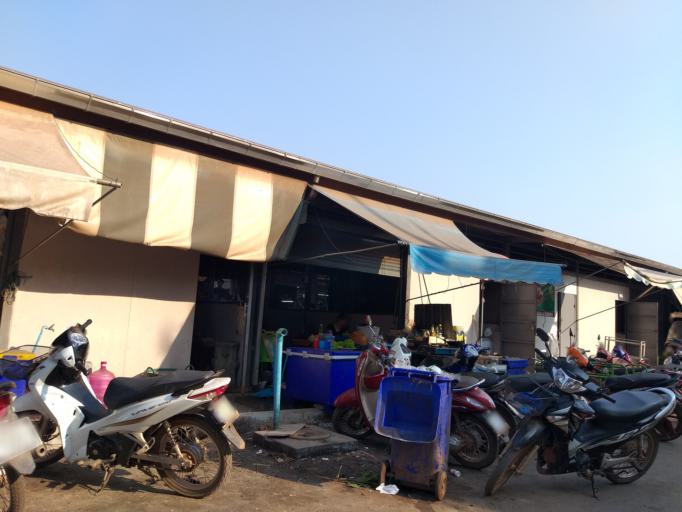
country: TH
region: Changwat Udon Thani
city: Ban Dung
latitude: 17.7436
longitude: 103.3590
